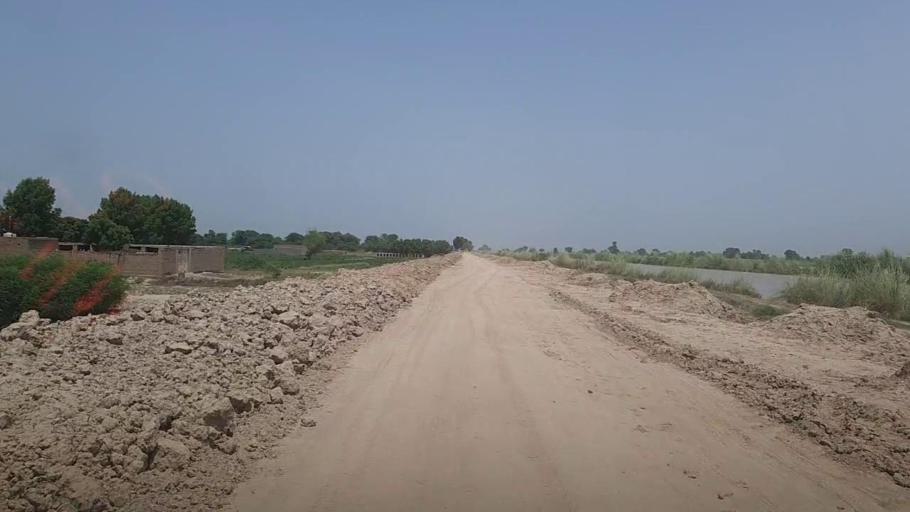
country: PK
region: Sindh
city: Pad Idan
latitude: 26.7877
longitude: 68.2769
